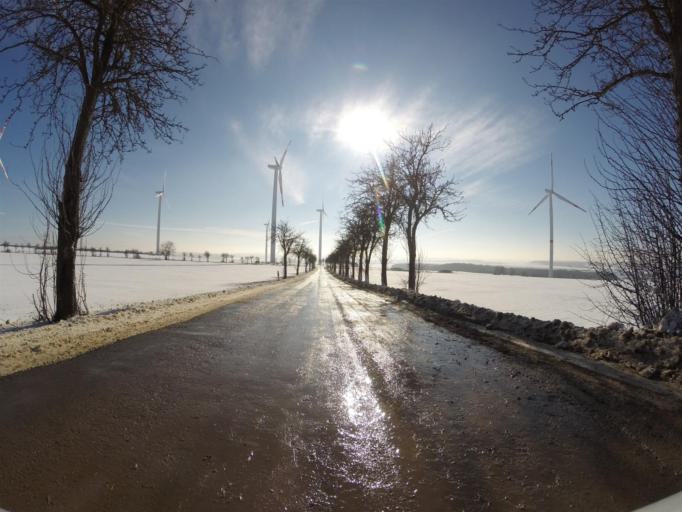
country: DE
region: Thuringia
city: Bucha
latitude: 50.9014
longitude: 11.5077
